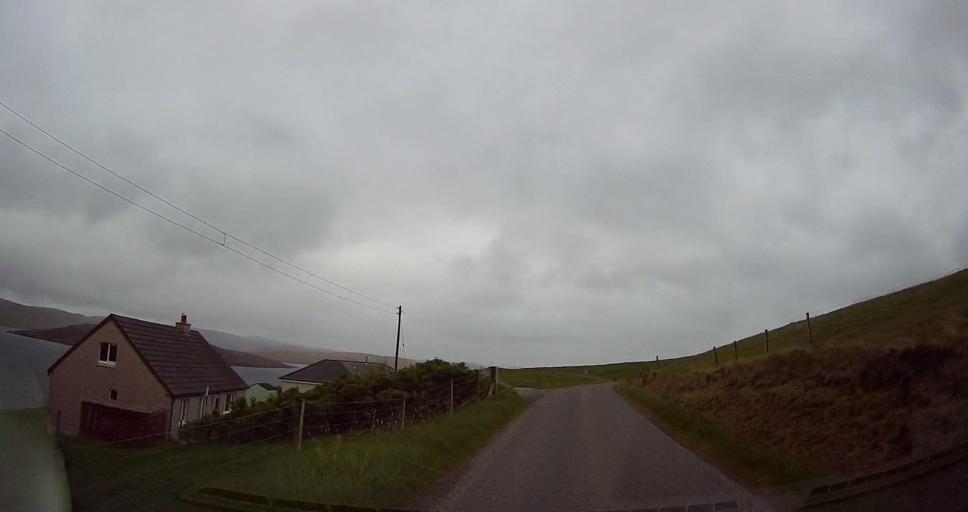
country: GB
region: Scotland
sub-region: Shetland Islands
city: Lerwick
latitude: 60.3700
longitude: -1.3822
